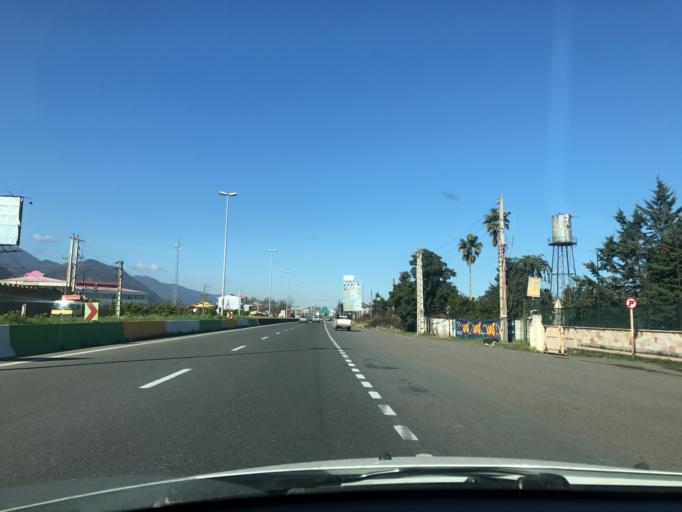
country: IR
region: Mazandaran
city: Ramsar
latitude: 36.9601
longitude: 50.6002
